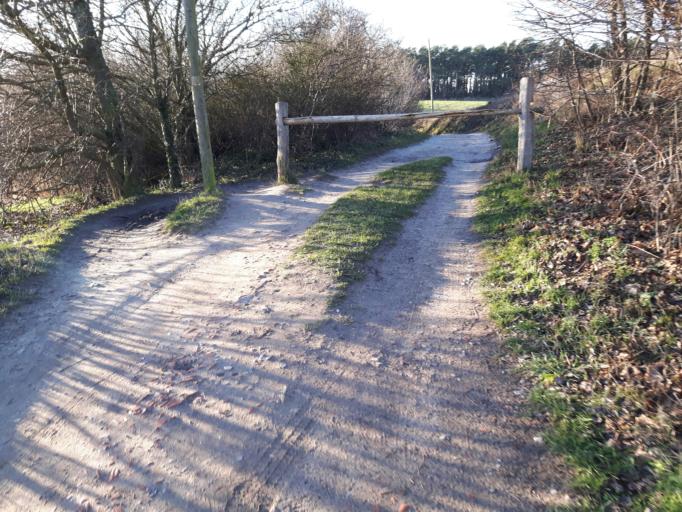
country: DE
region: Mecklenburg-Vorpommern
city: Ostseebad Binz
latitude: 54.3188
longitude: 13.6174
